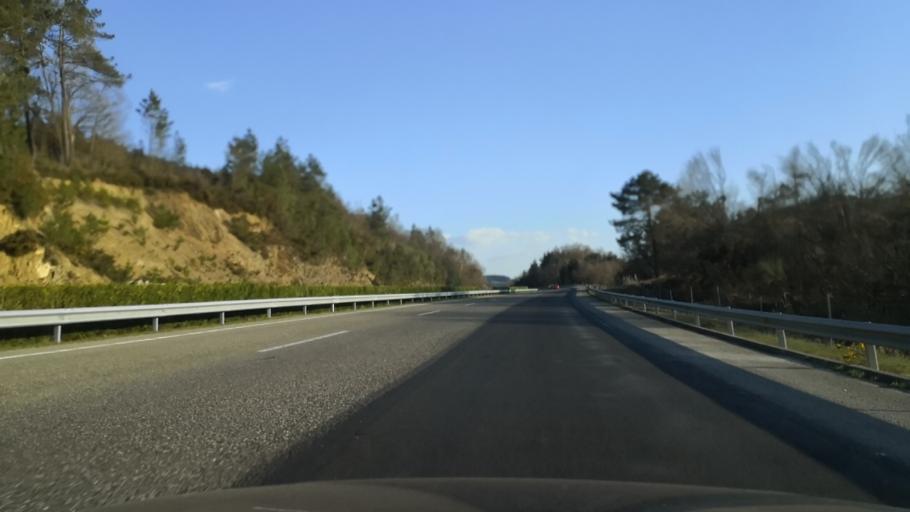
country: ES
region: Galicia
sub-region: Provincia de Lugo
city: Becerrea
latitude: 42.8992
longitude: -7.1879
